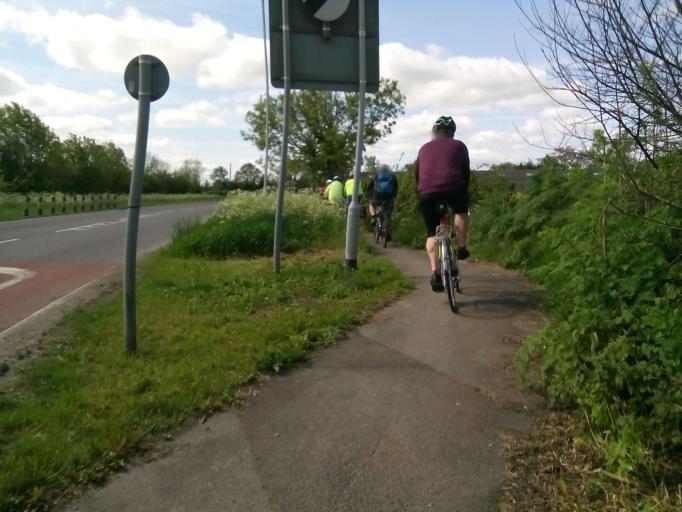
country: GB
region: England
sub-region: Cambridgeshire
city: Harston
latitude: 52.1346
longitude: 0.0739
